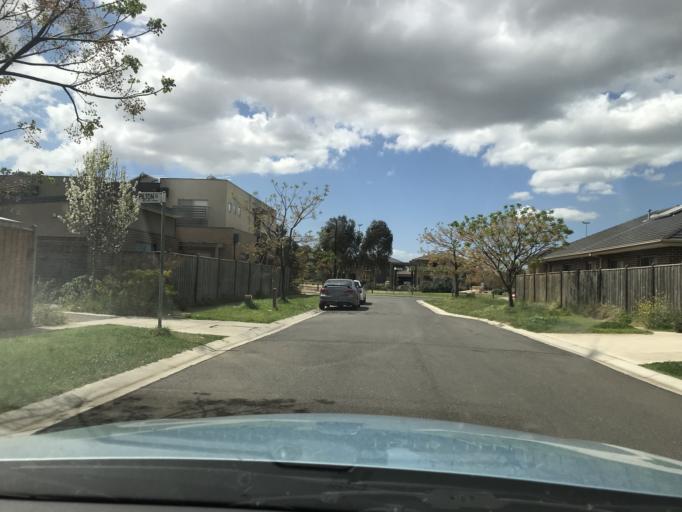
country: AU
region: Victoria
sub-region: Wyndham
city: Williams Landing
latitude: -37.8611
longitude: 144.7449
